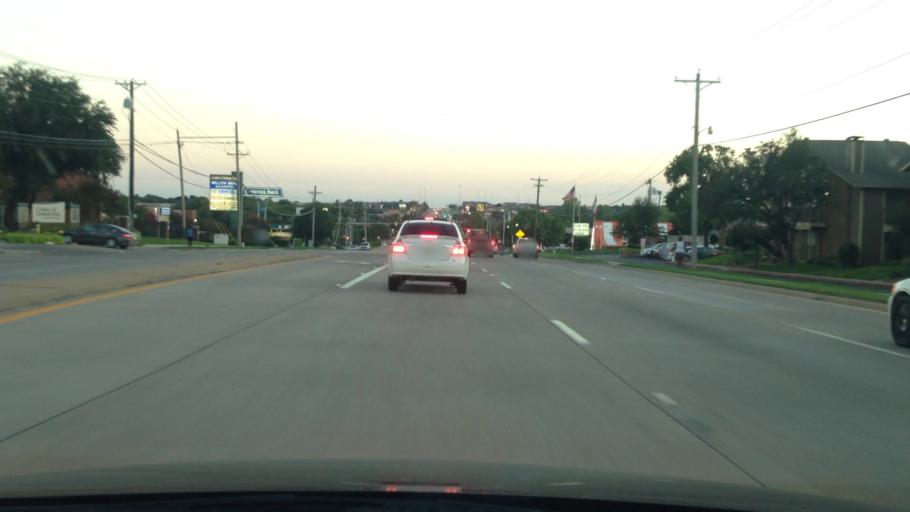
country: US
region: Texas
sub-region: Denton County
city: Lewisville
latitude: 33.0213
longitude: -96.9930
